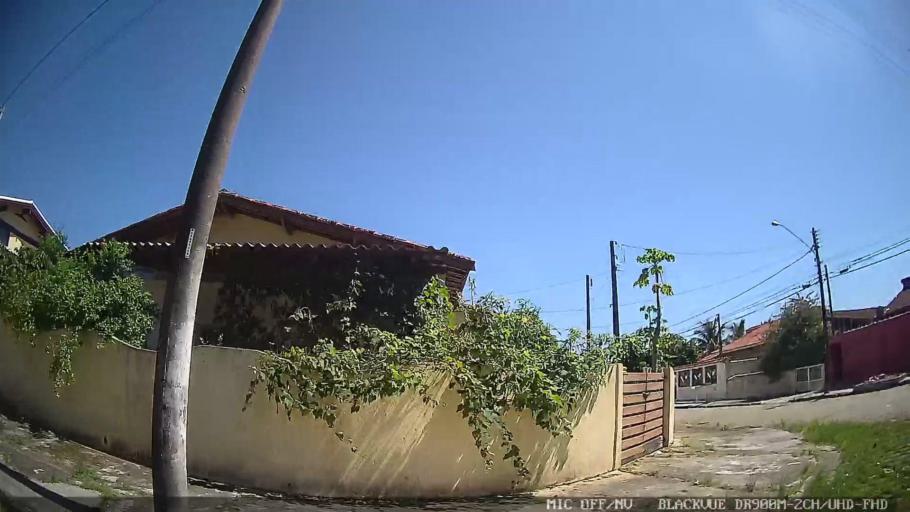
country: BR
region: Sao Paulo
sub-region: Peruibe
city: Peruibe
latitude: -24.3057
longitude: -46.9854
